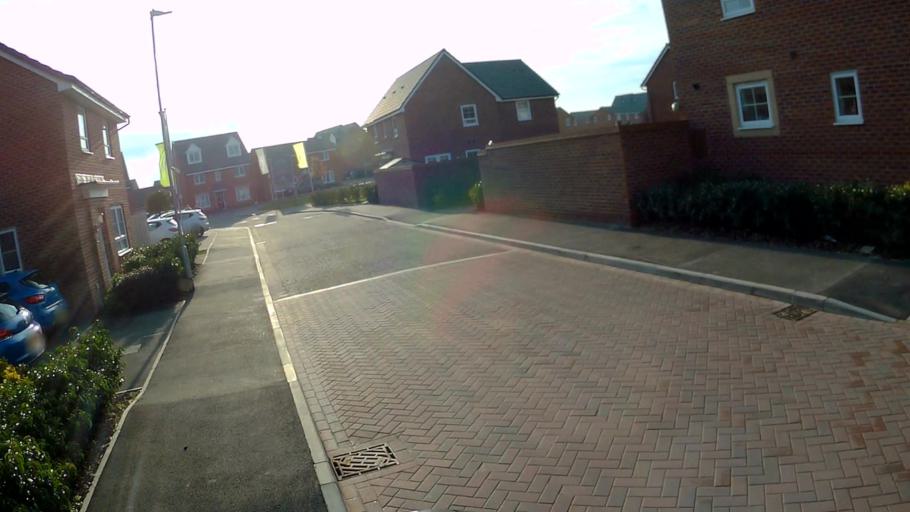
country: GB
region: England
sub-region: Lincolnshire
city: Bourne
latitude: 52.7589
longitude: -0.3867
